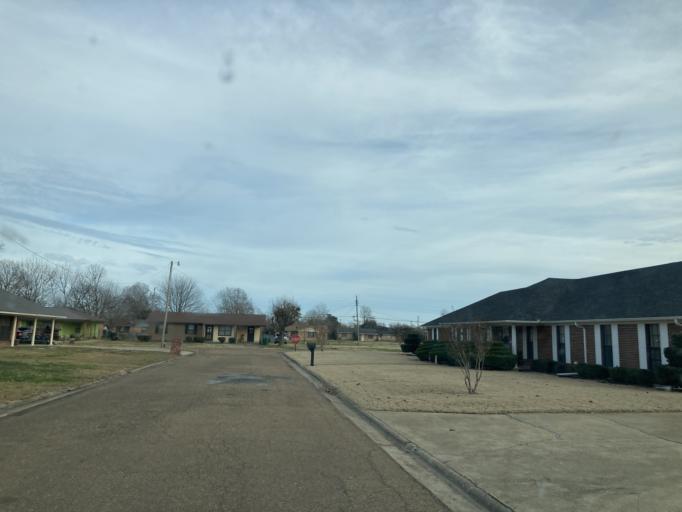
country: US
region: Mississippi
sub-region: Humphreys County
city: Belzoni
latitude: 33.1711
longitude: -90.5028
